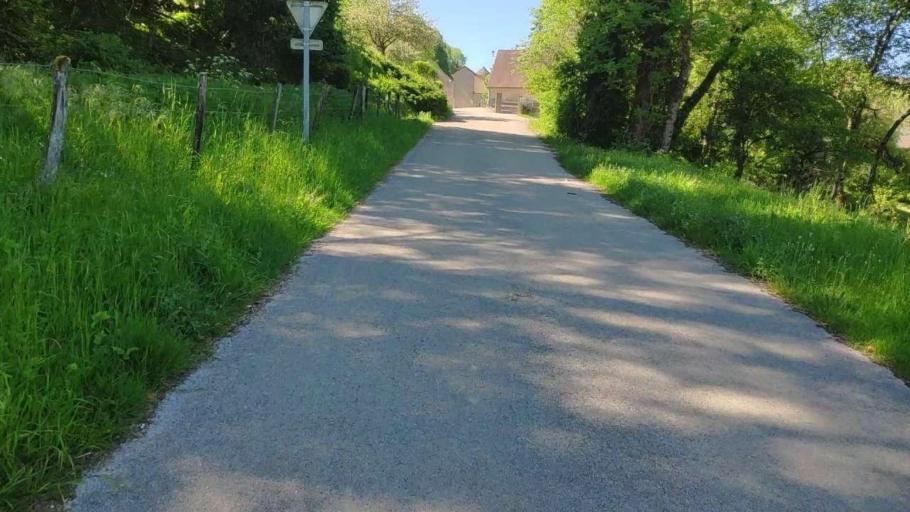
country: FR
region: Franche-Comte
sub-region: Departement du Jura
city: Clairvaux-les-Lacs
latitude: 46.7015
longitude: 5.7324
